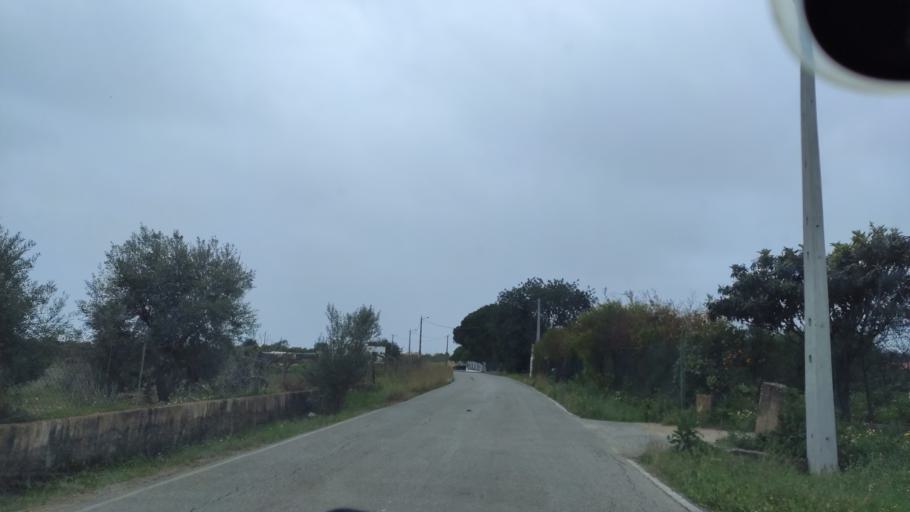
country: PT
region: Faro
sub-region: Faro
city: Santa Barbara de Nexe
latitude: 37.0816
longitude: -7.9253
